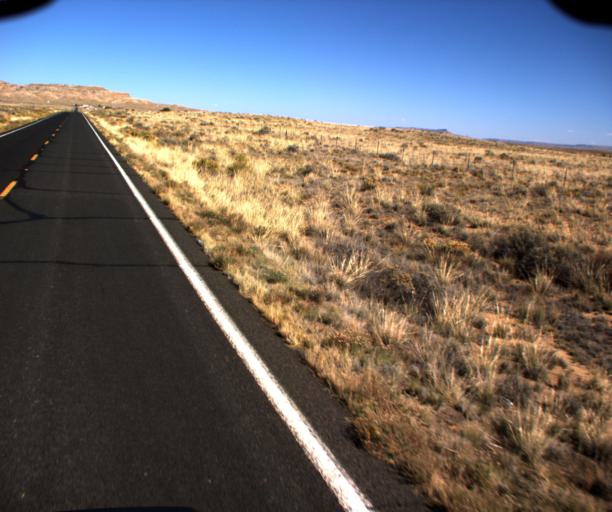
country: US
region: Arizona
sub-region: Navajo County
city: First Mesa
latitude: 35.7656
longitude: -110.5084
